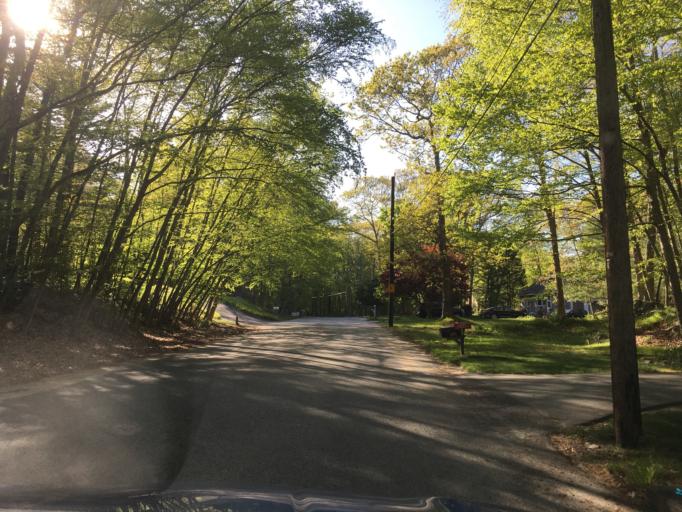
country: US
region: Rhode Island
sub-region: Washington County
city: Exeter
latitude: 41.6094
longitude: -71.5160
